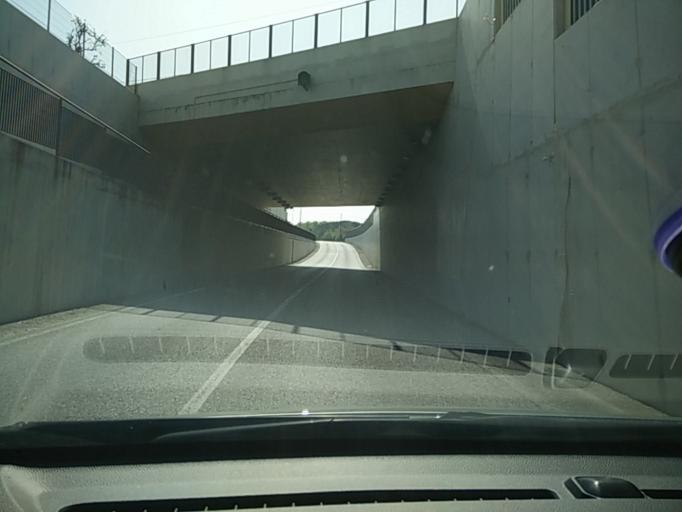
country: IT
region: Veneto
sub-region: Provincia di Venezia
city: Musile di Piave
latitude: 45.6308
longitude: 12.5312
